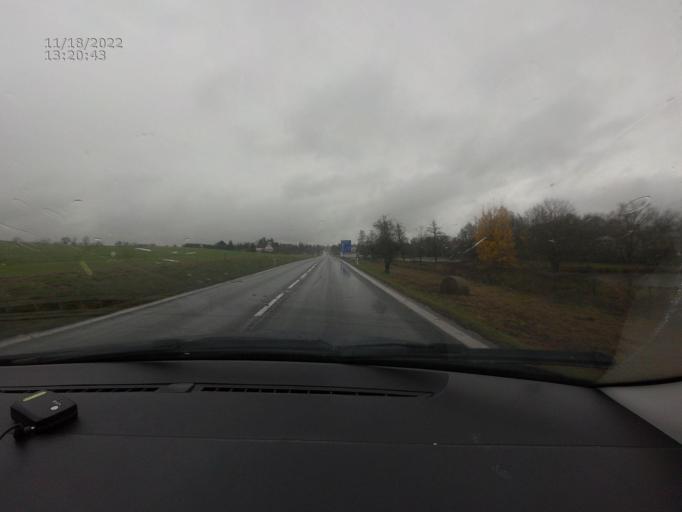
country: CZ
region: Plzensky
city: Horazd'ovice
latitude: 49.3267
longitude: 13.6767
